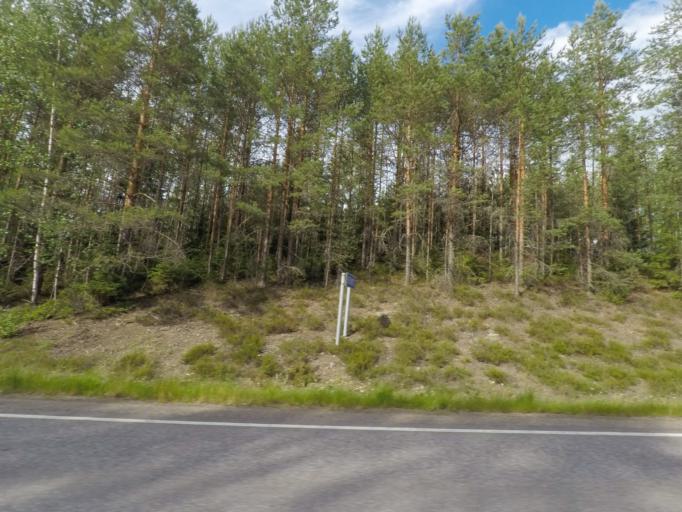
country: FI
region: Uusimaa
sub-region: Porvoo
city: Pukkila
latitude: 60.7714
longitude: 25.4547
